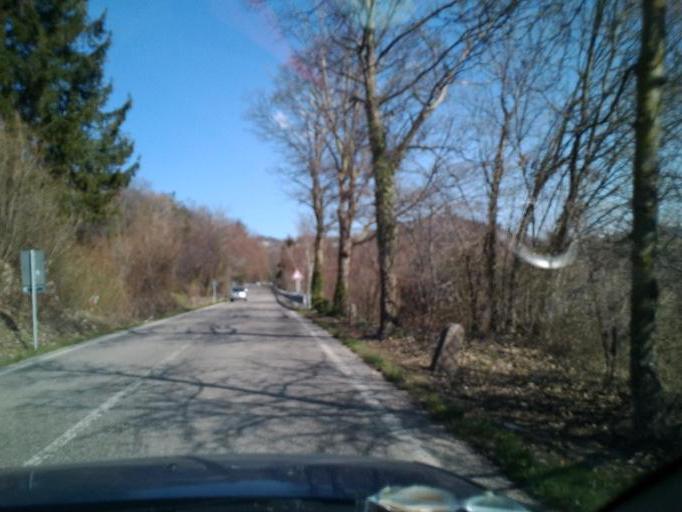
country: IT
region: Veneto
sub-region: Provincia di Verona
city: Bosco Chiesanuova
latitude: 45.5982
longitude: 11.0366
